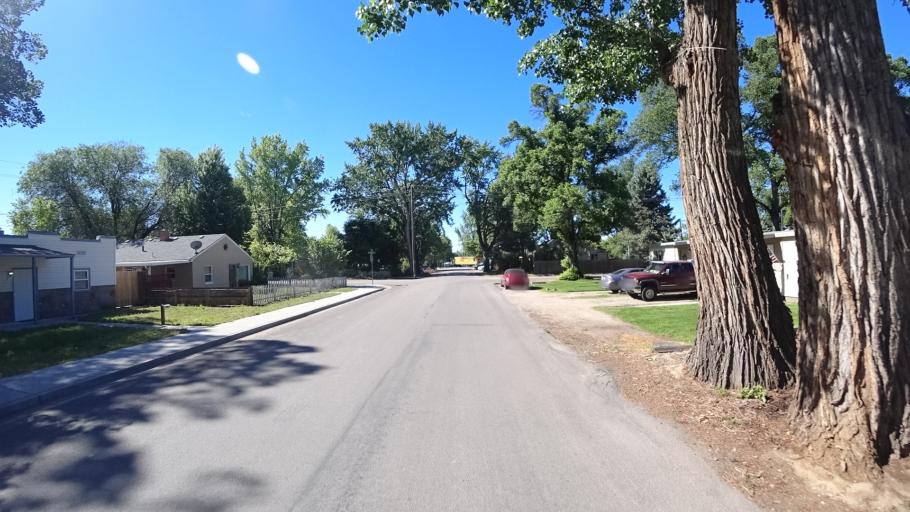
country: US
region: Idaho
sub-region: Ada County
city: Garden City
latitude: 43.6378
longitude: -116.2283
